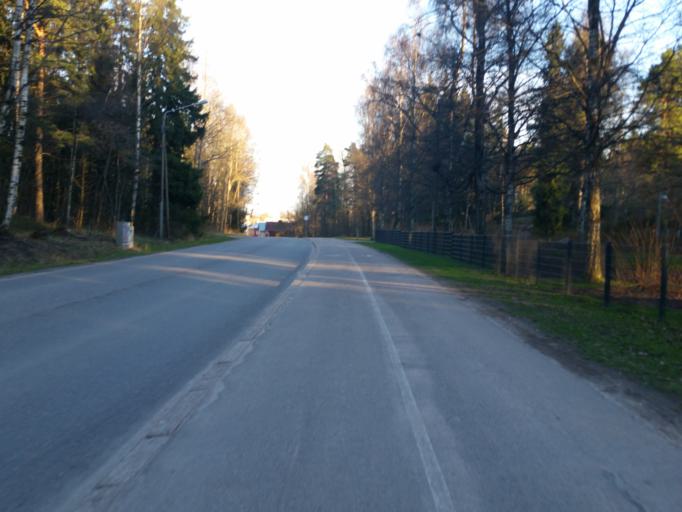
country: FI
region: Uusimaa
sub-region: Helsinki
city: Helsinki
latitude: 60.2120
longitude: 24.9601
